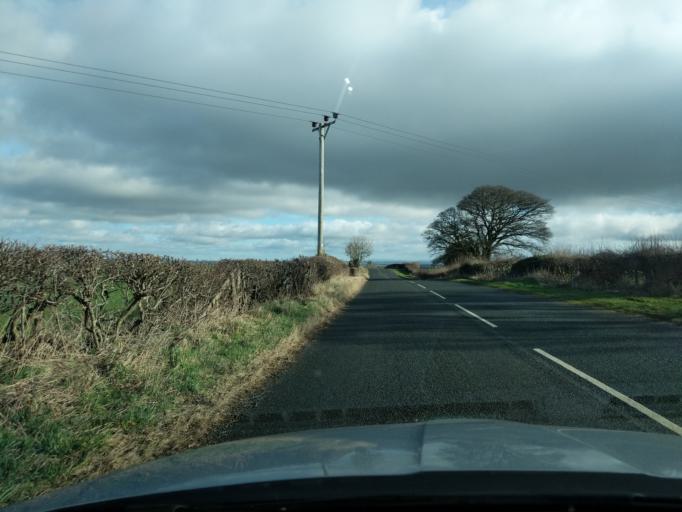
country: GB
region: England
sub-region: North Yorkshire
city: Catterick Garrison
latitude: 54.3517
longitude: -1.6830
